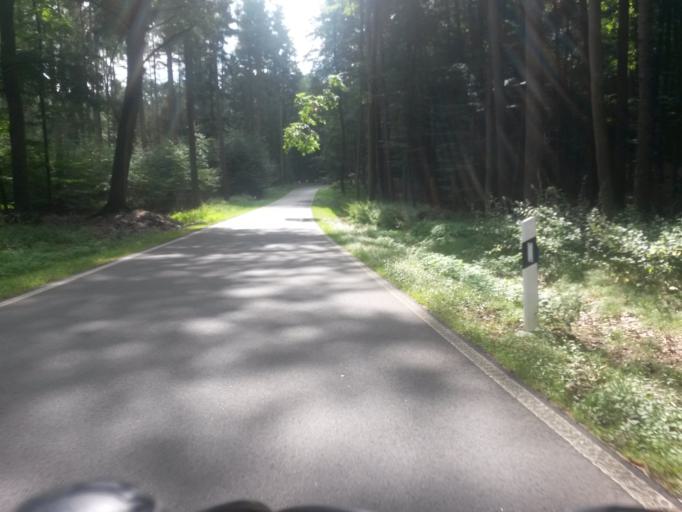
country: DE
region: Brandenburg
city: Angermunde
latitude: 53.0444
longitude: 13.9044
